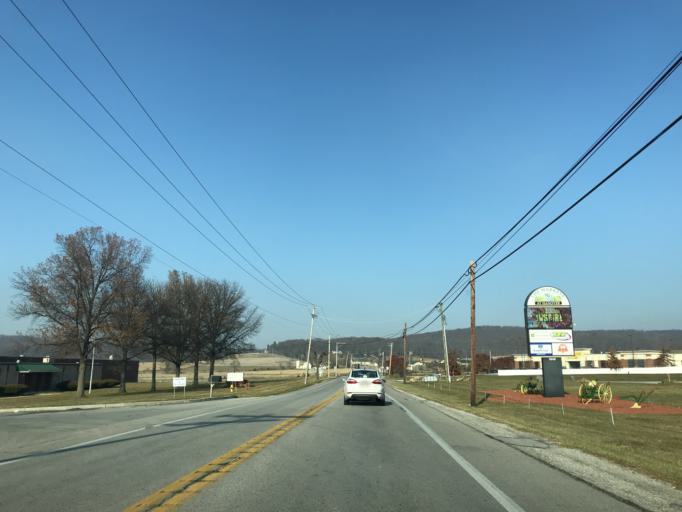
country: US
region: Pennsylvania
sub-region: York County
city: Hanover
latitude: 39.8312
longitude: -76.9728
